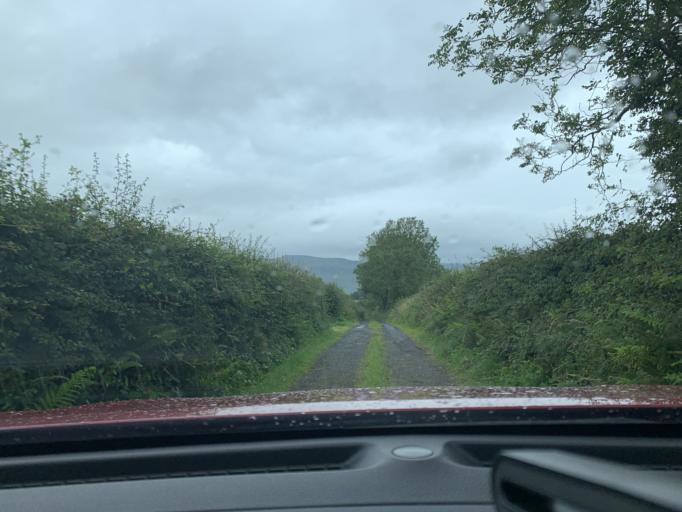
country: IE
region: Connaught
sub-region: Sligo
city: Sligo
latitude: 54.3061
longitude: -8.4453
